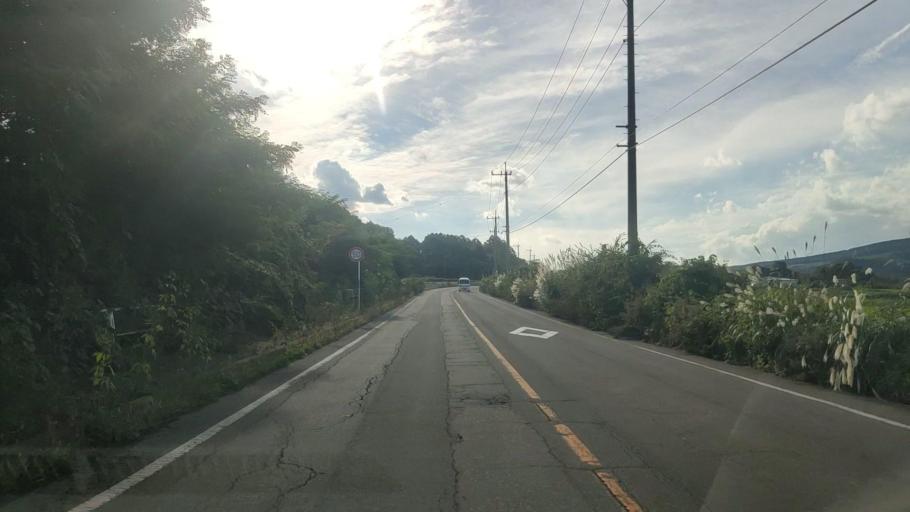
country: JP
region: Nagano
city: Komoro
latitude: 36.4853
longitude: 138.4611
